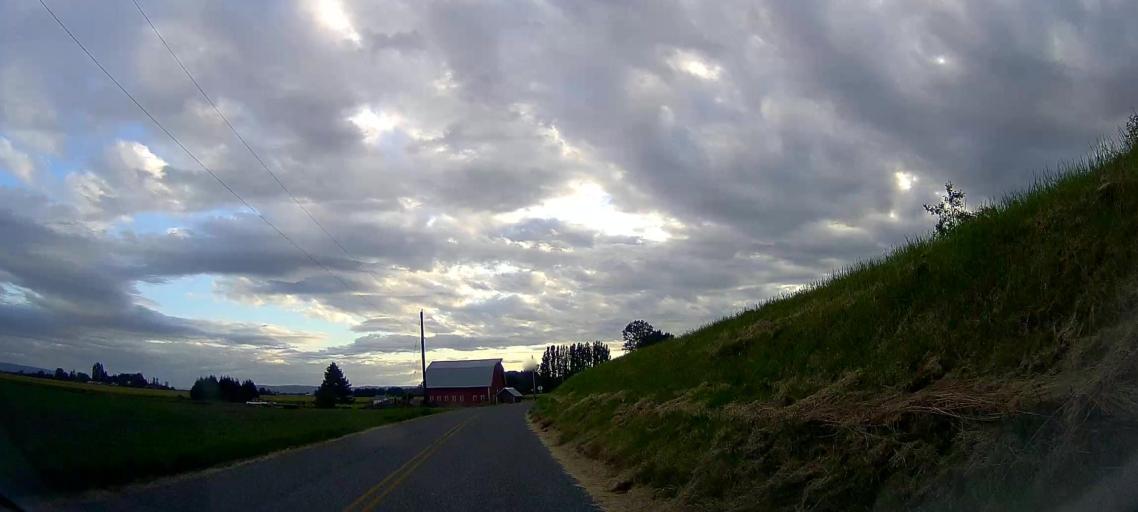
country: US
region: Washington
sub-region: Skagit County
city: Mount Vernon
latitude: 48.3683
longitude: -122.3966
